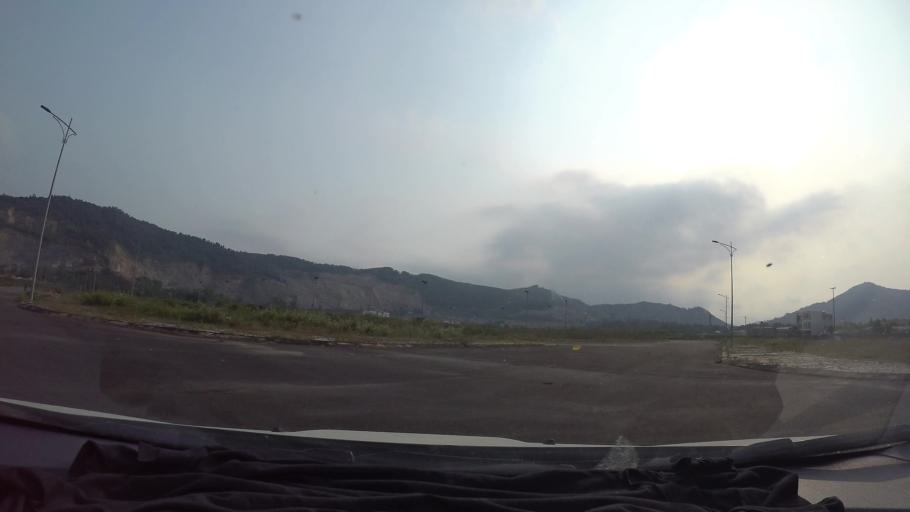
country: VN
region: Da Nang
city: Lien Chieu
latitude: 16.0479
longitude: 108.1592
